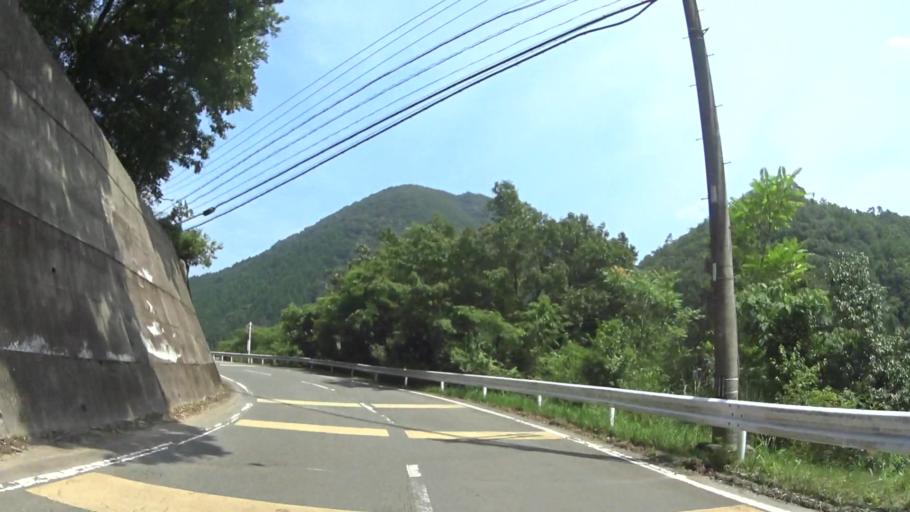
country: JP
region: Kyoto
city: Ayabe
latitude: 35.2810
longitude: 135.4299
